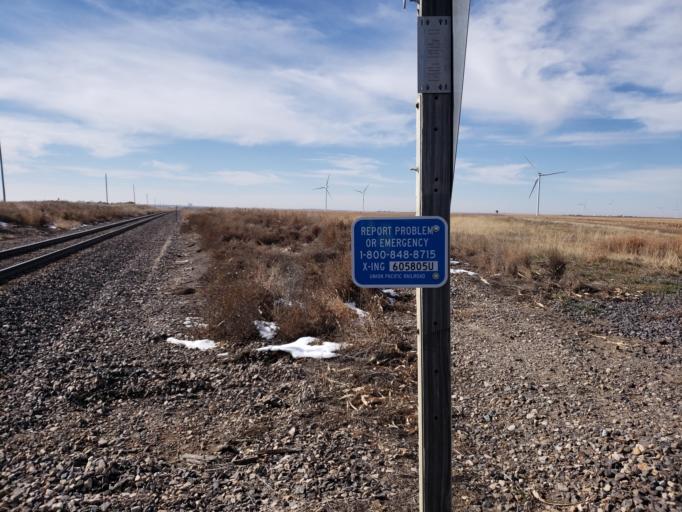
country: US
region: Kansas
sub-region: Ford County
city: Dodge City
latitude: 37.4713
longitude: -99.9432
